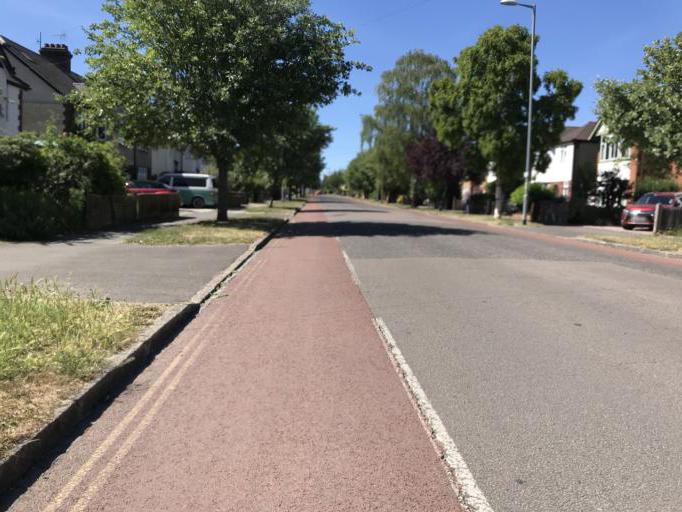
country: GB
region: England
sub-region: Cambridgeshire
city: Cambridge
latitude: 52.2193
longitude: 0.1219
